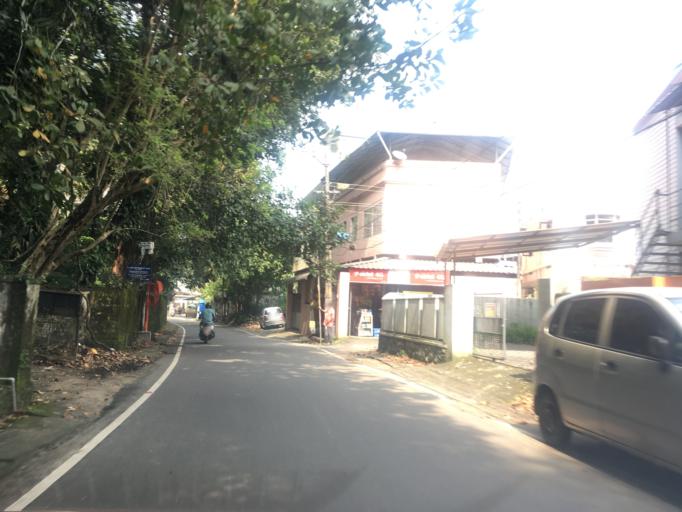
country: IN
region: Kerala
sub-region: Ernakulam
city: Elur
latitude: 10.0359
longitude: 76.3077
